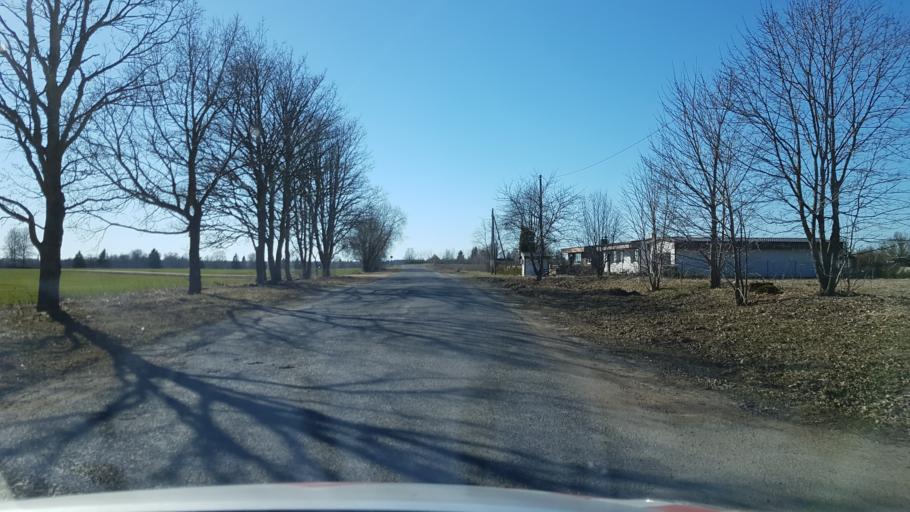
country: EE
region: Laeaene-Virumaa
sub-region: Kadrina vald
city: Kadrina
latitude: 59.4421
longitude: 26.1260
